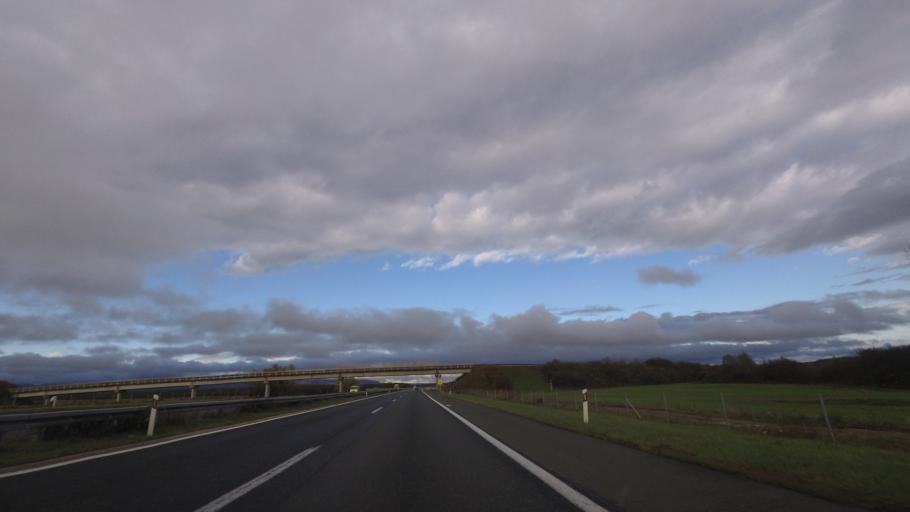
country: HR
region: Zagrebacka
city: Jastrebarsko
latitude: 45.6021
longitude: 15.6357
